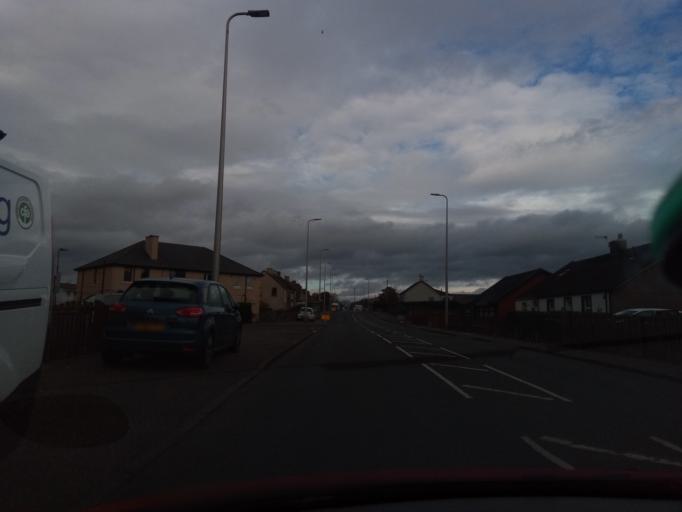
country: GB
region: Scotland
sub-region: West Lothian
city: Blackburn
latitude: 55.8727
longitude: -3.6235
